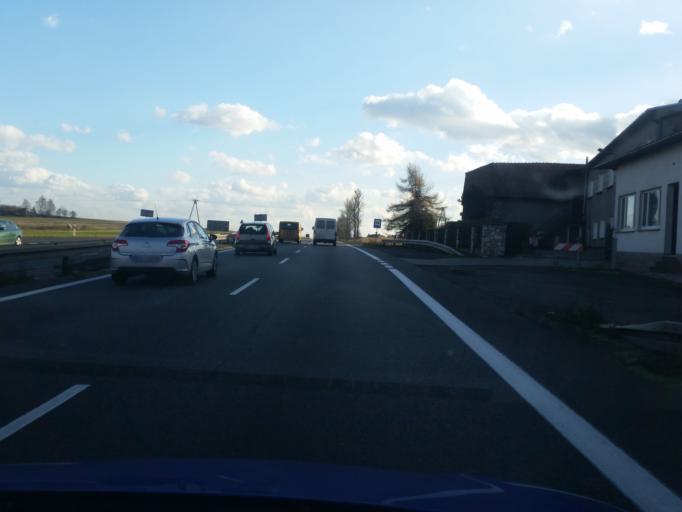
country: PL
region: Silesian Voivodeship
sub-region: Powiat bedzinski
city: Siewierz
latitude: 50.5056
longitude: 19.1973
